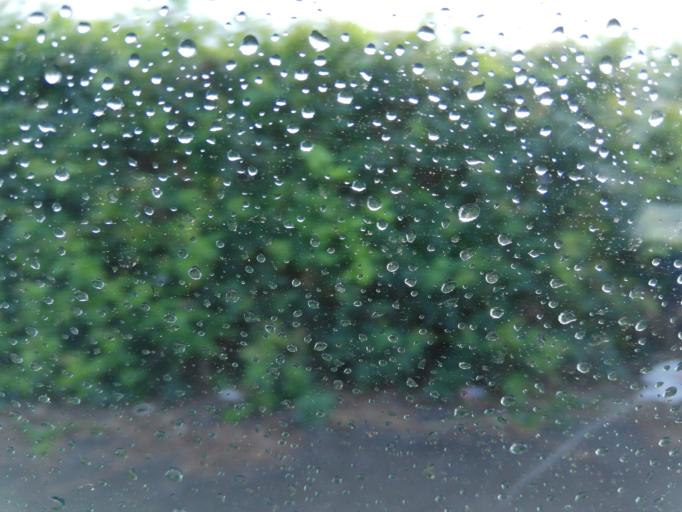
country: MU
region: Plaines Wilhems
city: Ebene
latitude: -20.2428
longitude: 57.4818
